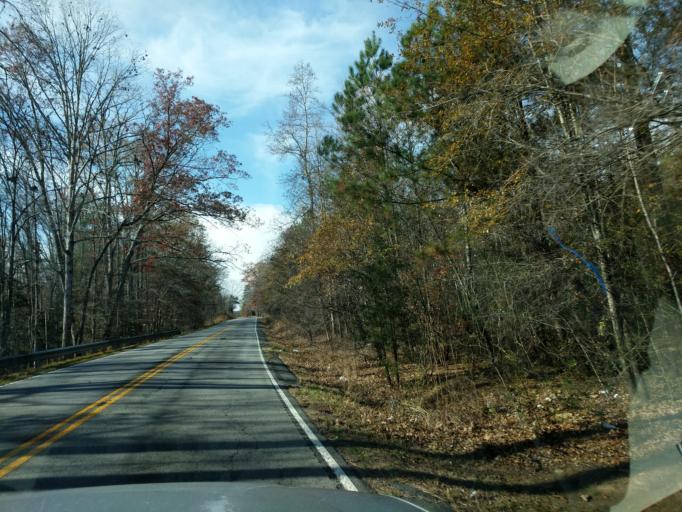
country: US
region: South Carolina
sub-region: Pickens County
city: Pickens
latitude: 34.8615
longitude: -82.7700
